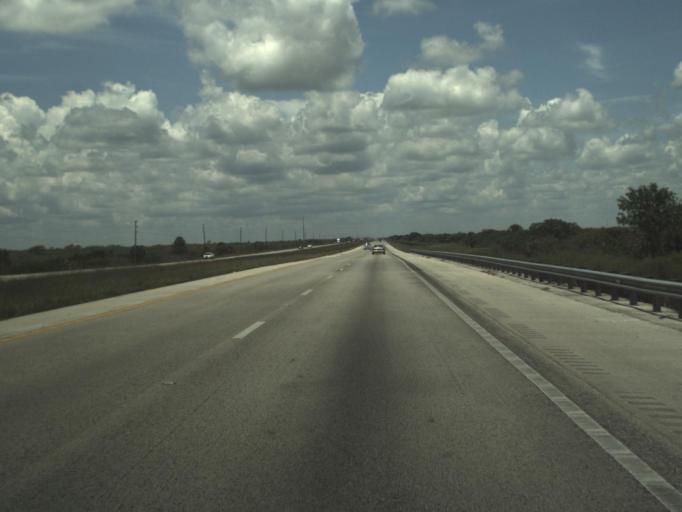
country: US
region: Florida
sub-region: Broward County
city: Weston
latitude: 26.1566
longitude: -80.7638
